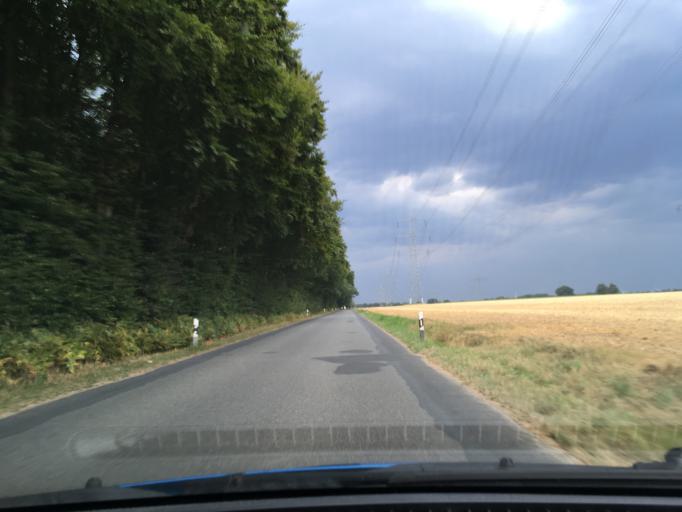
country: DE
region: Lower Saxony
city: Hanstedt Eins
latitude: 53.0828
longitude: 10.3875
